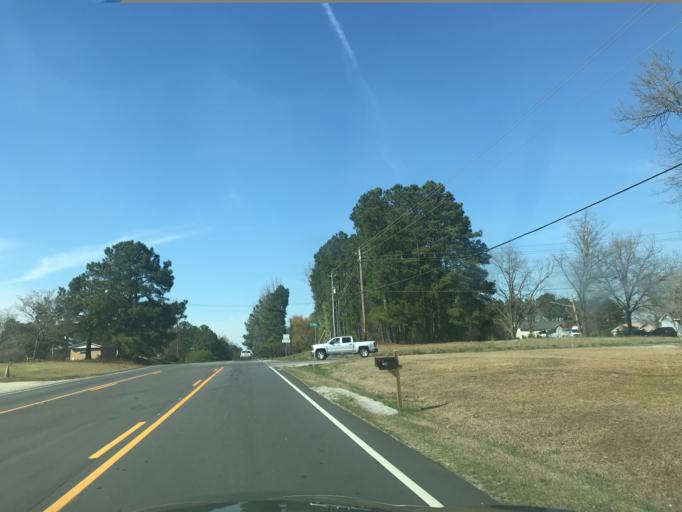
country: US
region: North Carolina
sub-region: Wake County
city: Fuquay-Varina
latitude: 35.5618
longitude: -78.7547
